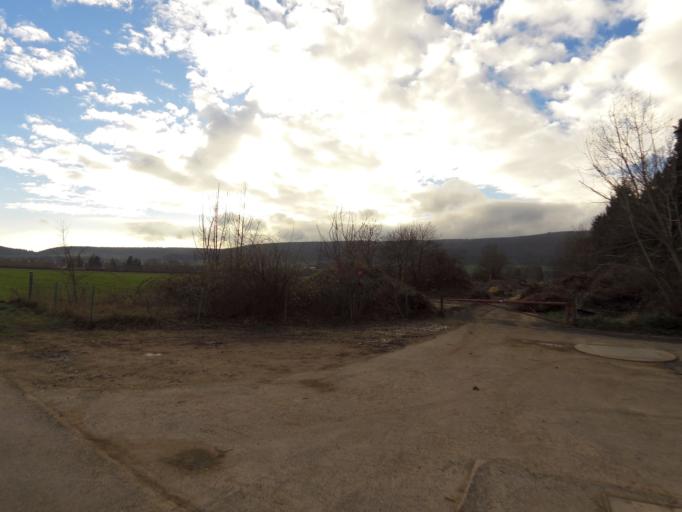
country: DE
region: Lower Saxony
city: Buhren
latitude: 51.4894
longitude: 9.6100
